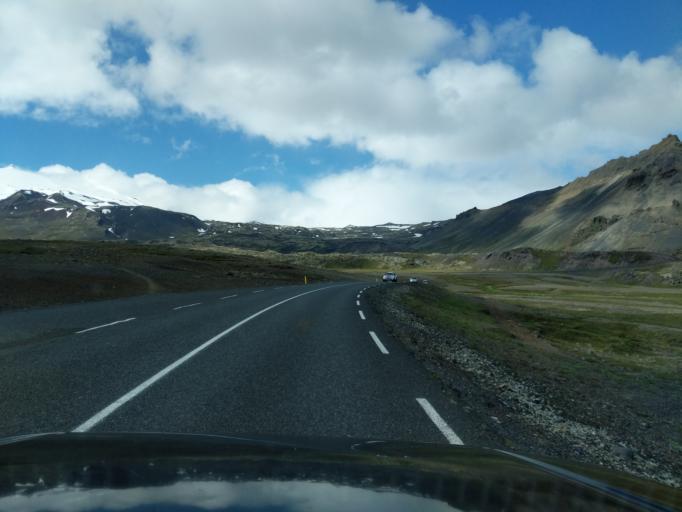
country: IS
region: West
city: Olafsvik
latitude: 64.7560
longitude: -23.6705
